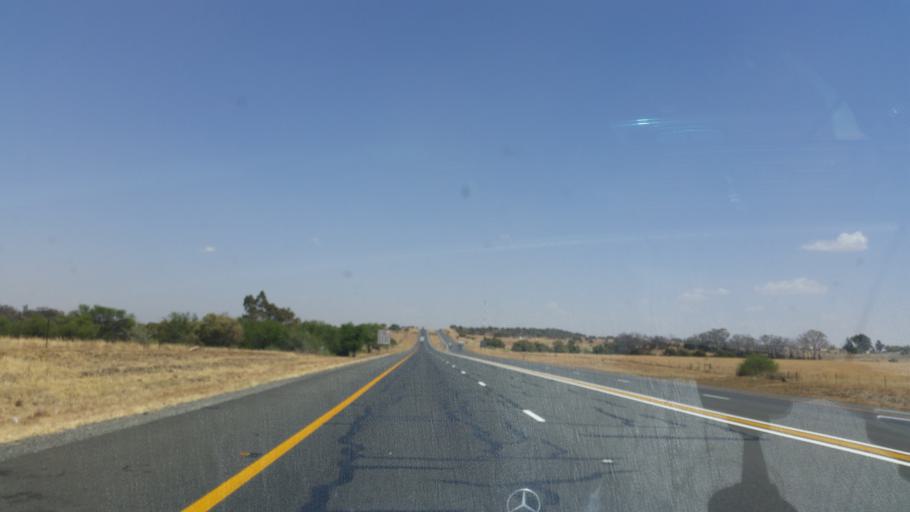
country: ZA
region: Orange Free State
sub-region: Lejweleputswa District Municipality
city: Brandfort
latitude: -28.9010
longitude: 26.4694
